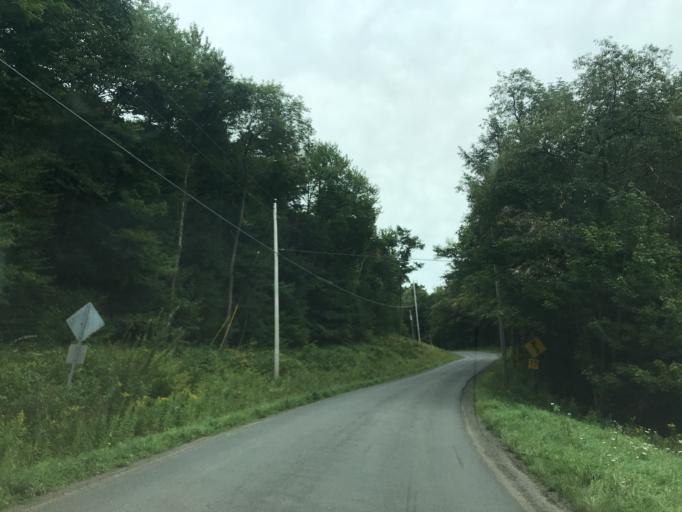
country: US
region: New York
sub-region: Otsego County
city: Worcester
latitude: 42.5897
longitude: -74.6799
